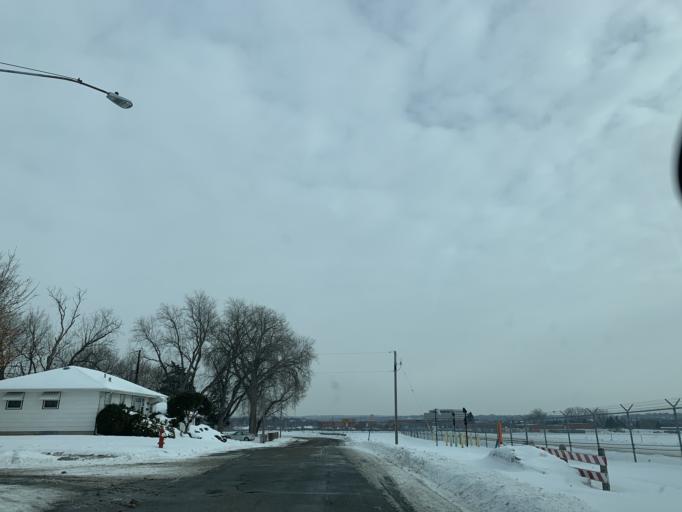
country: US
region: Minnesota
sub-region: Dakota County
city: Mendota Heights
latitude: 44.8963
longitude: -93.2092
